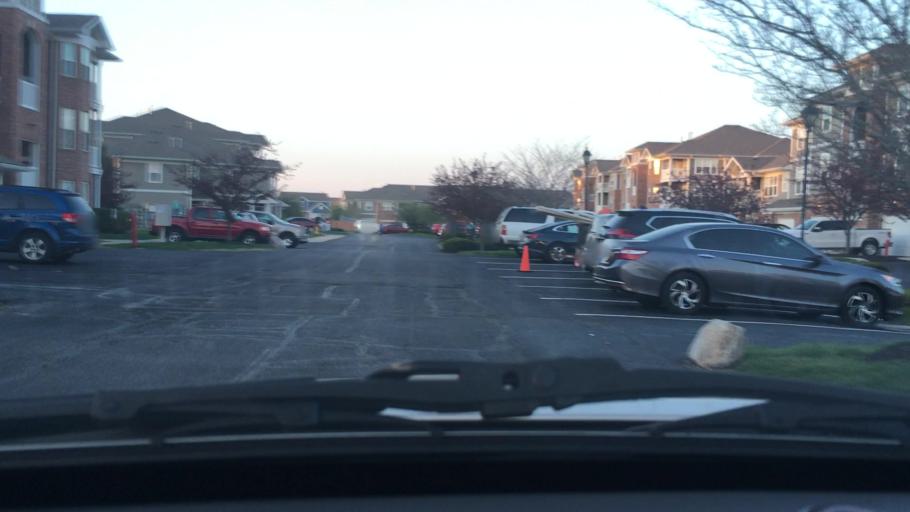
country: US
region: Indiana
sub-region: Hamilton County
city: Westfield
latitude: 40.0394
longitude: -86.1691
